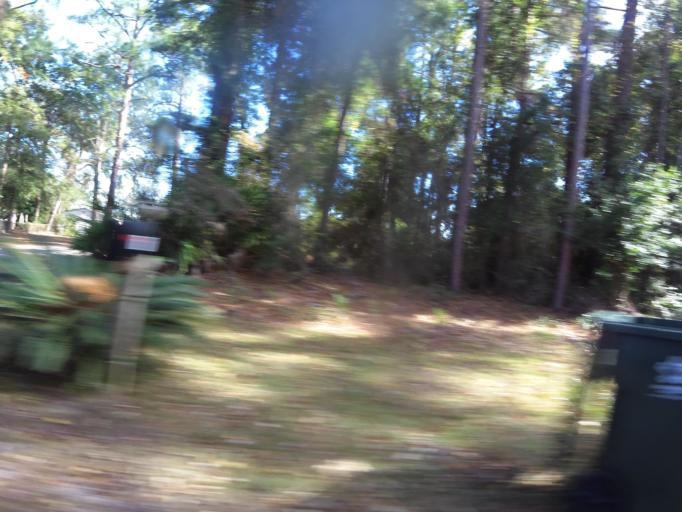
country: US
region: Georgia
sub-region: Glynn County
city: Brunswick
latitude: 31.1253
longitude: -81.5534
